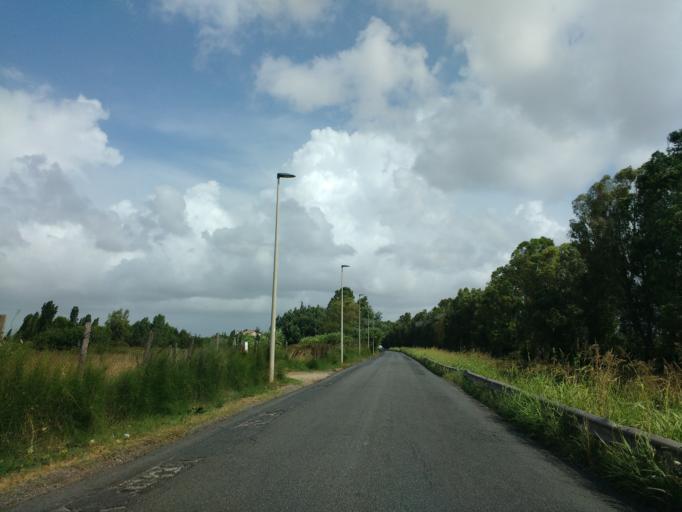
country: IT
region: Latium
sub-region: Citta metropolitana di Roma Capitale
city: Acilia-Castel Fusano-Ostia Antica
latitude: 41.7572
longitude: 12.3299
